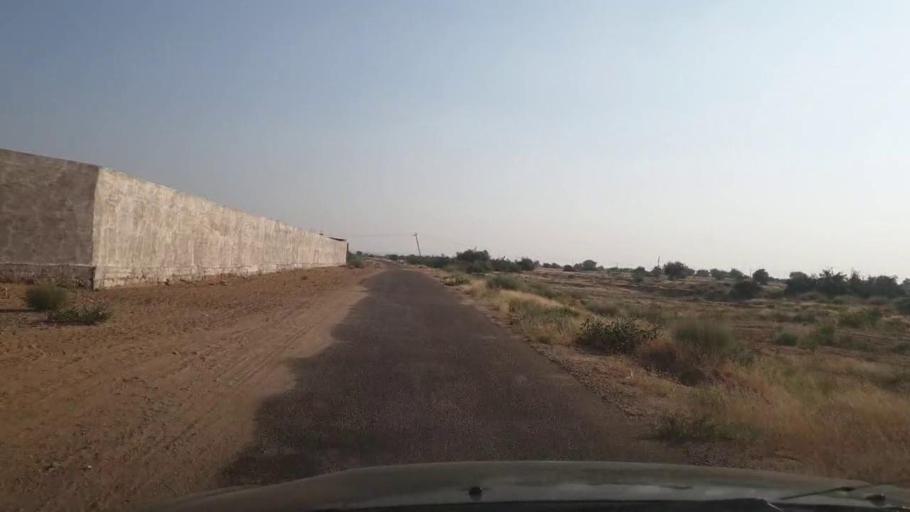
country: PK
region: Sindh
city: Jamshoro
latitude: 25.3476
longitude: 67.8379
